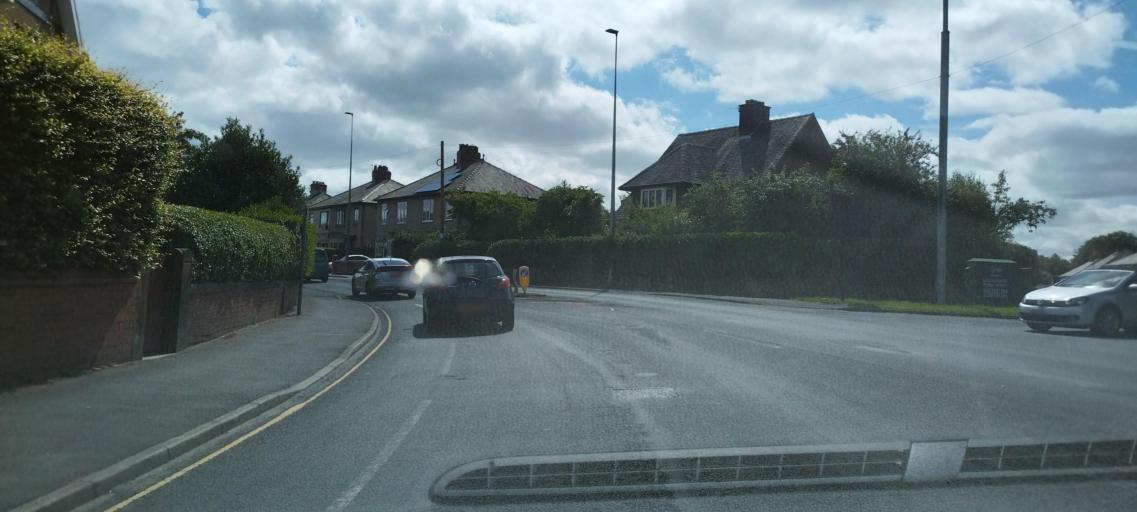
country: GB
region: England
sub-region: Blackburn with Darwen
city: Blackburn
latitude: 53.7362
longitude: -2.5172
